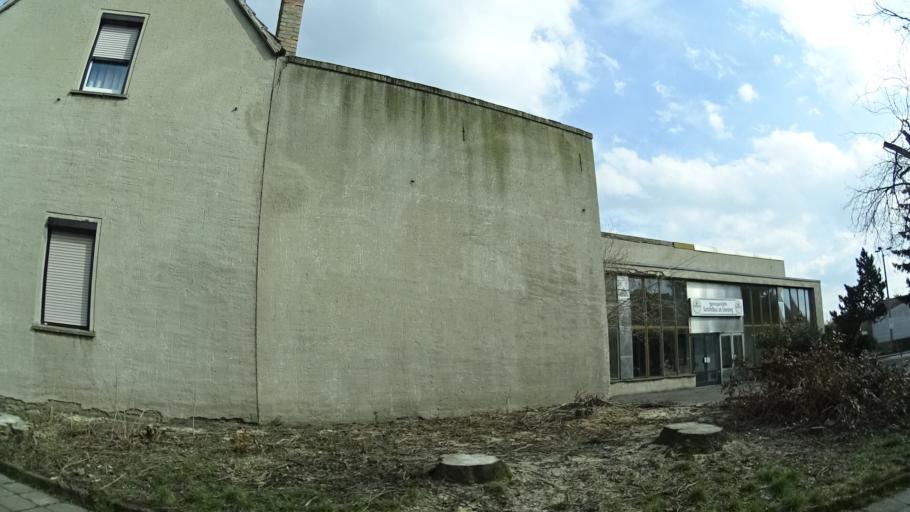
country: DE
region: Saxony-Anhalt
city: Naumburg
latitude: 51.1537
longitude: 11.8284
